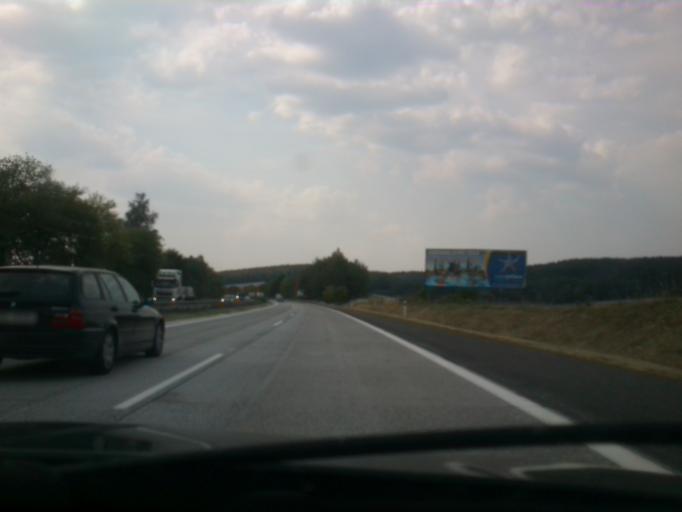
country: CZ
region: Central Bohemia
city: Divisov
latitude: 49.8315
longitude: 14.8595
